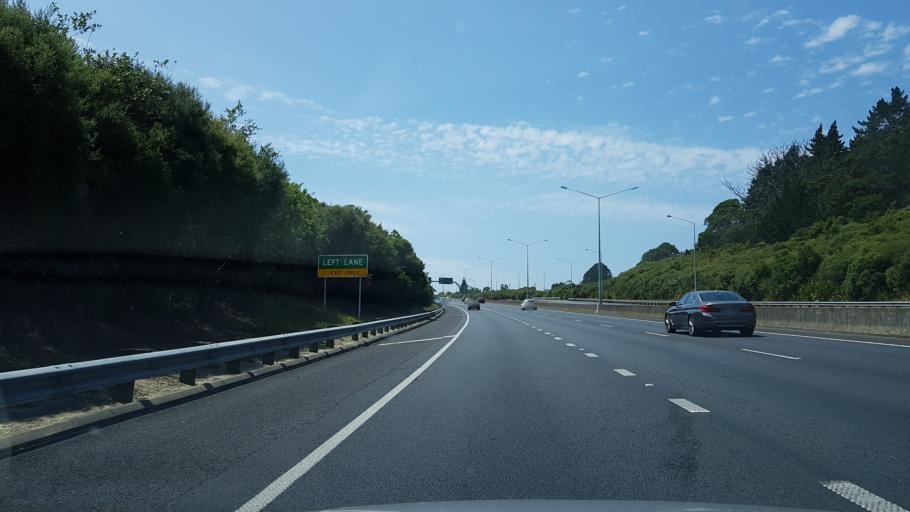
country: NZ
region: Auckland
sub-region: Auckland
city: Rothesay Bay
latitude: -36.7623
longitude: 174.6989
